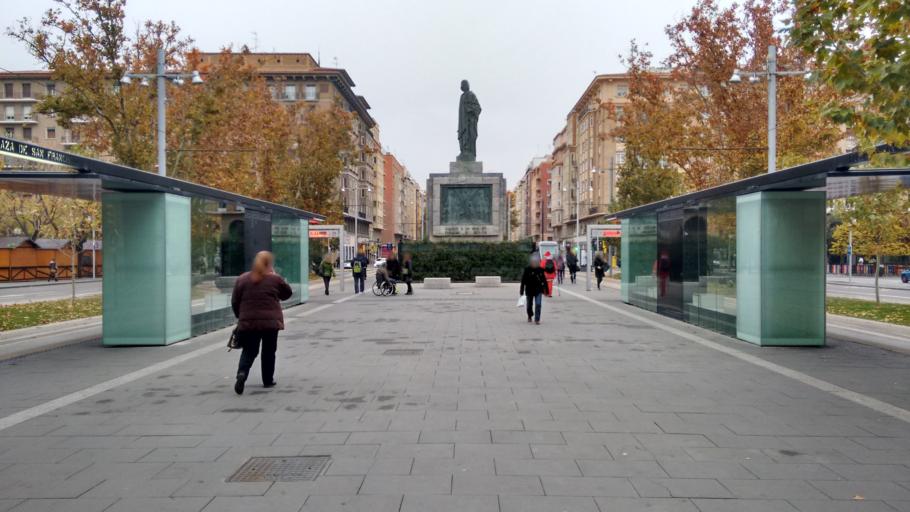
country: ES
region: Aragon
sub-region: Provincia de Zaragoza
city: Delicias
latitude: 41.6407
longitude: -0.8954
